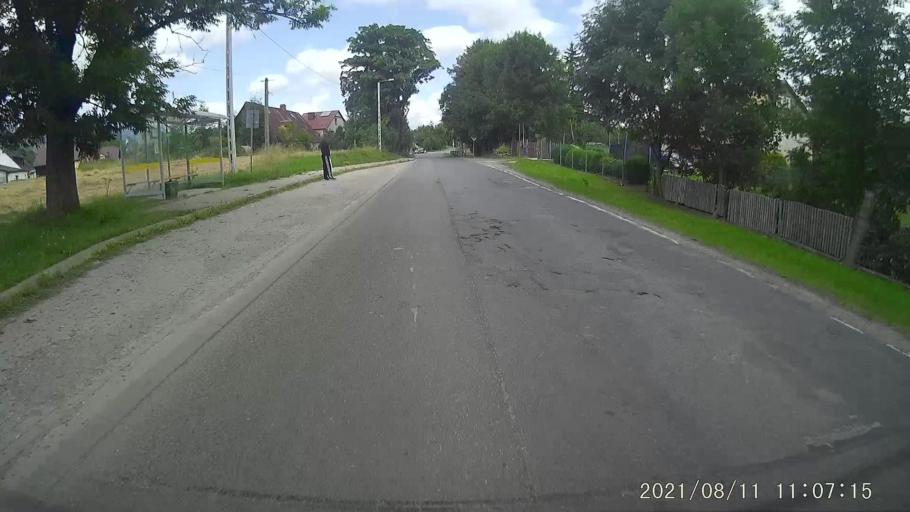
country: PL
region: Lower Silesian Voivodeship
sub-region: Powiat klodzki
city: Bystrzyca Klodzka
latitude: 50.3298
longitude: 16.6034
